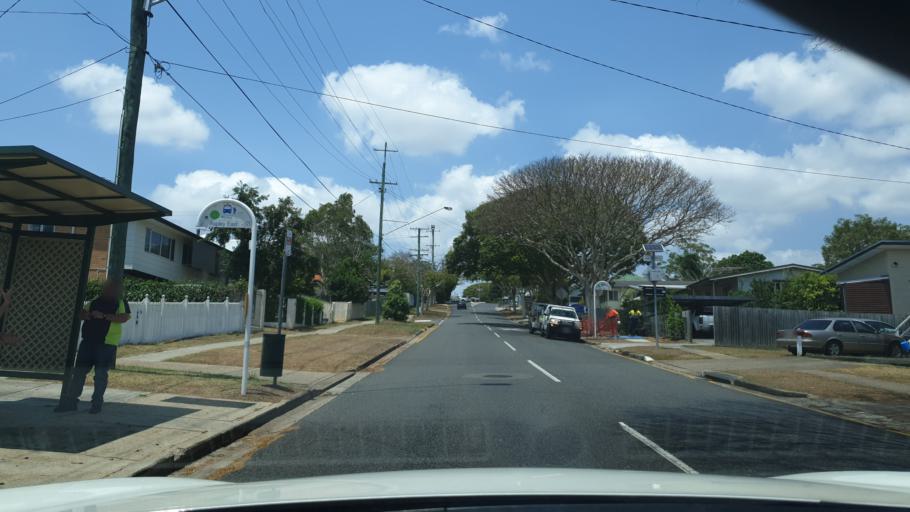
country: AU
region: Queensland
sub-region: Brisbane
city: Zillmere
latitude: -27.3636
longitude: 153.0268
